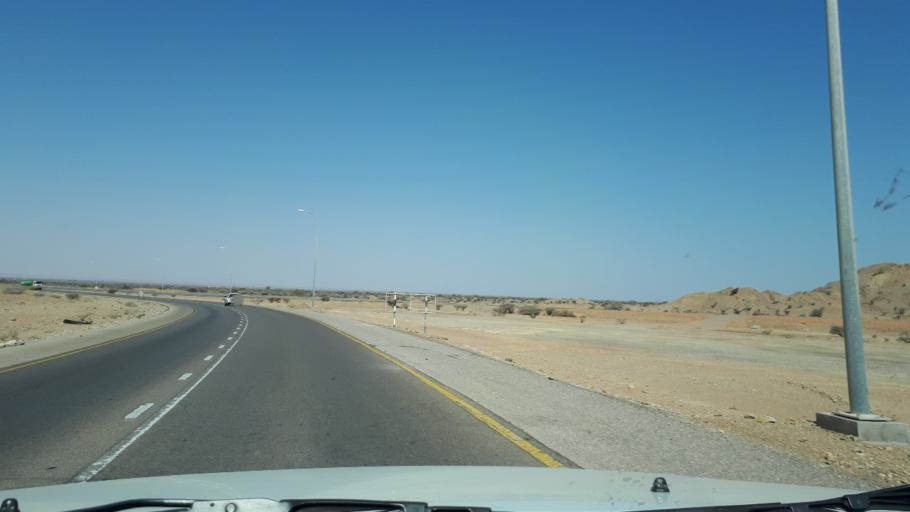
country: OM
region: Ash Sharqiyah
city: Sur
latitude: 22.3157
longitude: 59.2970
